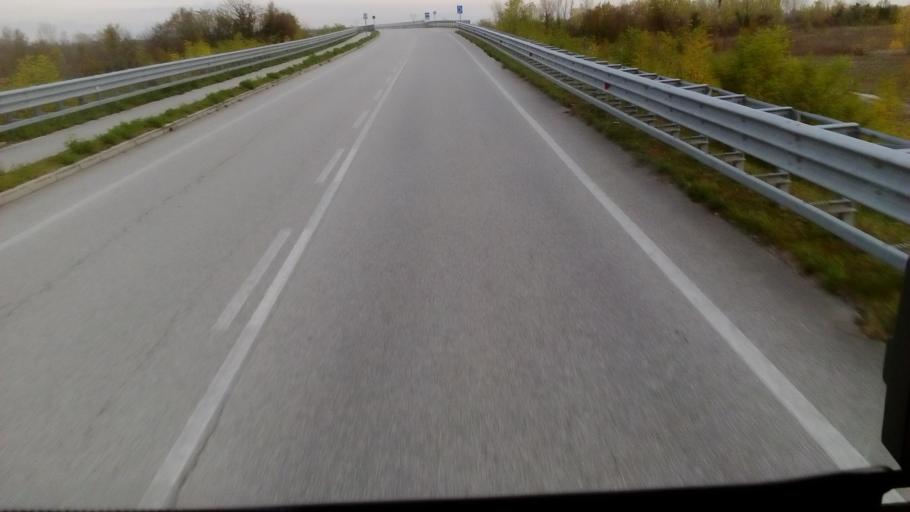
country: IT
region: Friuli Venezia Giulia
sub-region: Provincia di Pordenone
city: Vivaro
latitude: 46.0931
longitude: 12.8010
